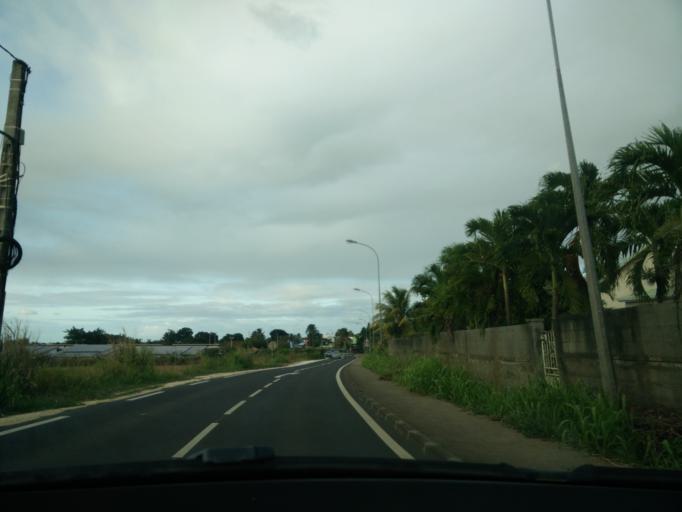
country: GP
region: Guadeloupe
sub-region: Guadeloupe
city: Baie-Mahault
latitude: 16.2372
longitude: -61.6041
